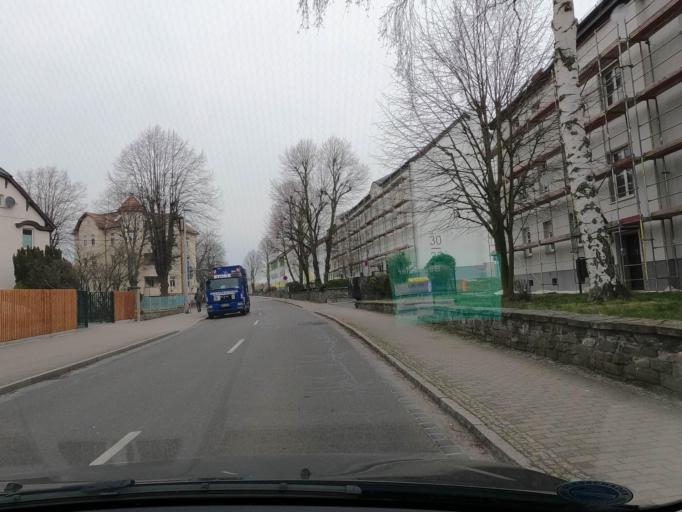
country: DE
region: Saxony
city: Schkeuditz
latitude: 51.3973
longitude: 12.2262
